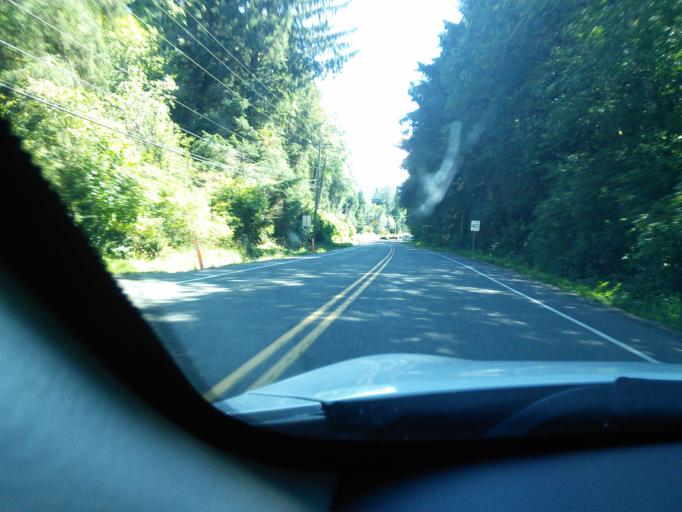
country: CA
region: British Columbia
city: Campbell River
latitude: 50.3244
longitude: -125.9222
